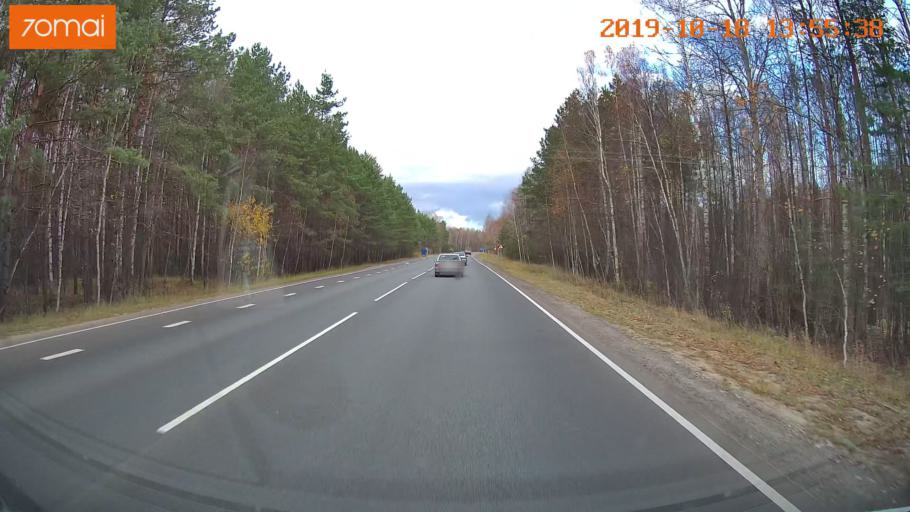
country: RU
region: Rjazan
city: Spas-Klepiki
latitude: 55.0544
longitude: 40.0242
